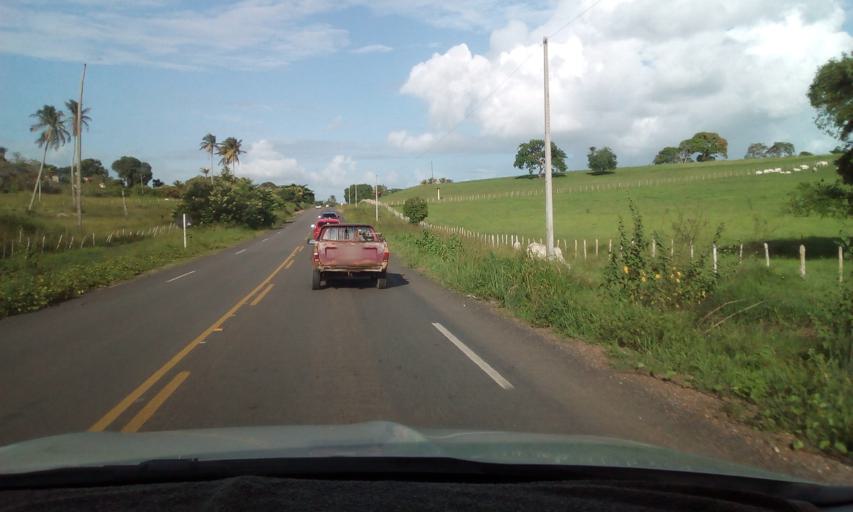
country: BR
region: Paraiba
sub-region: Mamanguape
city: Mamanguape
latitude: -6.8162
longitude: -35.2280
